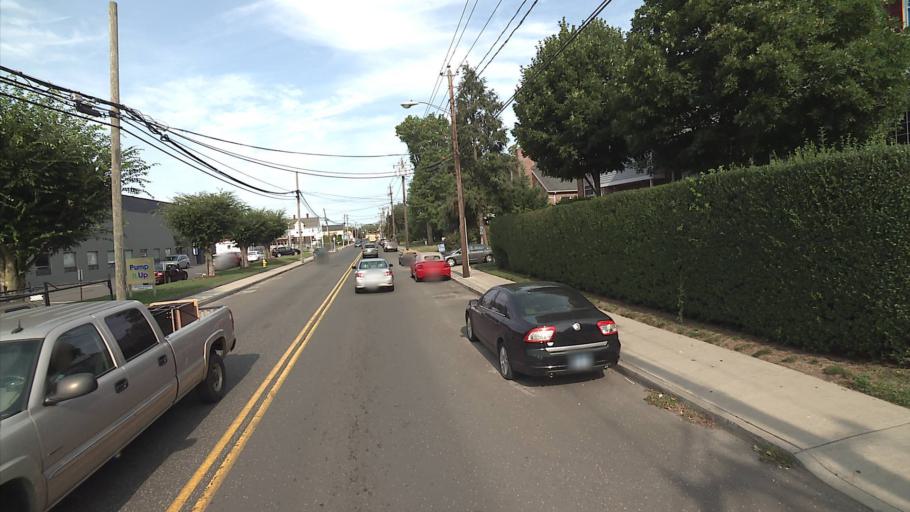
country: US
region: Connecticut
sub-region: Fairfield County
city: Norwalk
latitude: 41.1246
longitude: -73.4170
